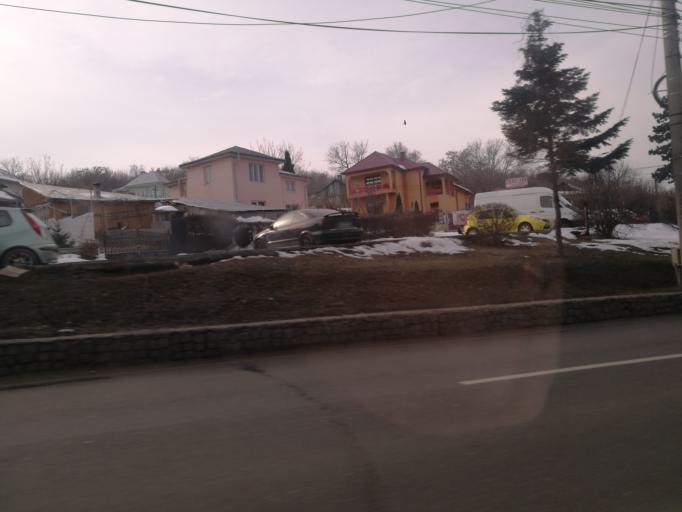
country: RO
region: Suceava
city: Suceava
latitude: 47.6490
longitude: 26.2629
